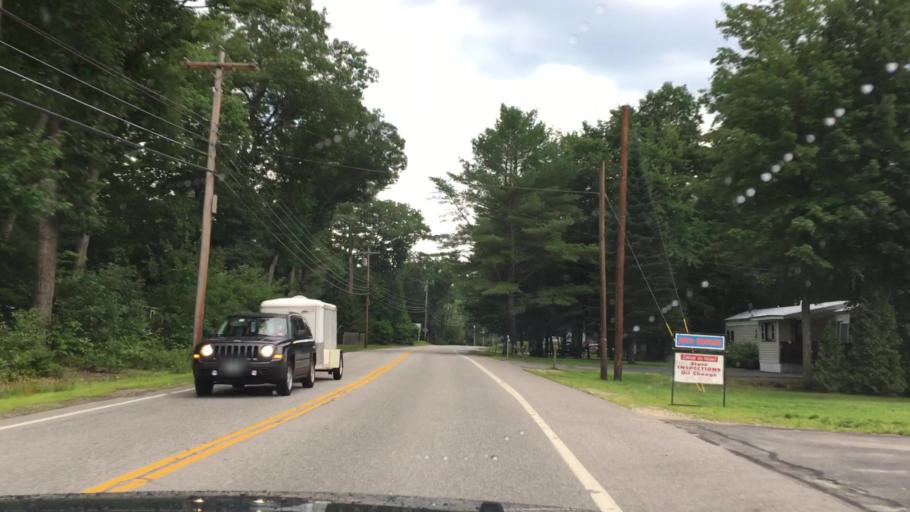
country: US
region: New Hampshire
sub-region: Belknap County
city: Meredith
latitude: 43.6739
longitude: -71.5059
